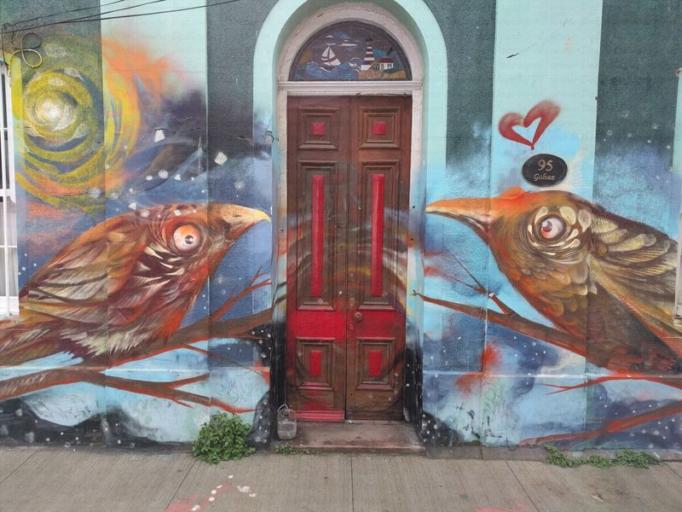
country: CL
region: Valparaiso
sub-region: Provincia de Valparaiso
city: Valparaiso
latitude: -33.0414
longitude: -71.6282
